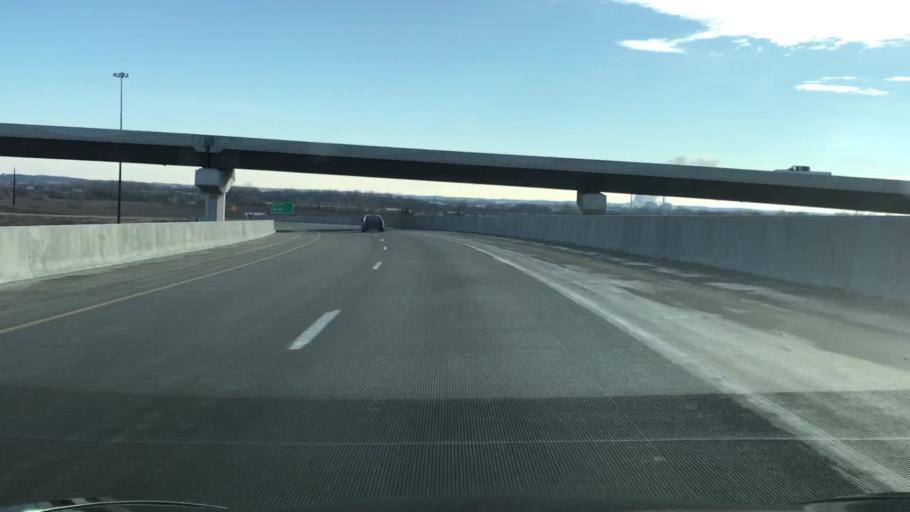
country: US
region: Iowa
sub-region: Pottawattamie County
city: Council Bluffs
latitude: 41.2325
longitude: -95.8974
